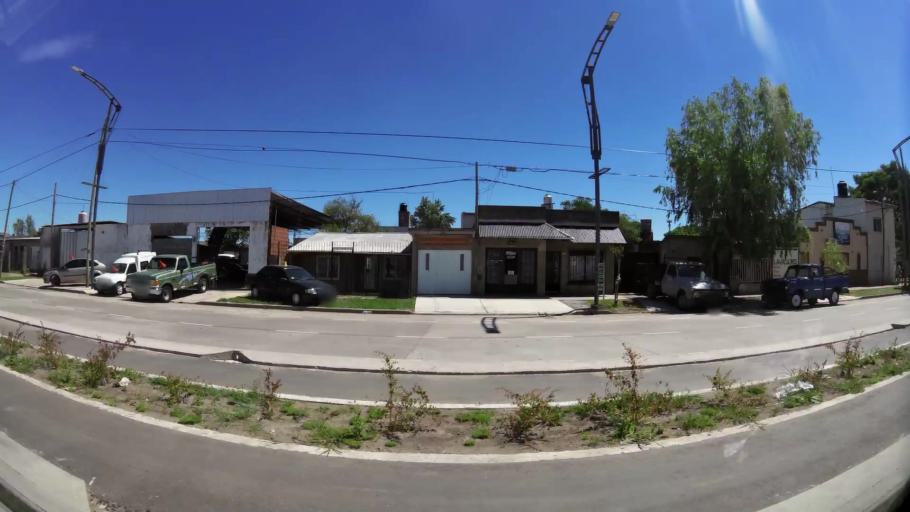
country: AR
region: Santa Fe
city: Perez
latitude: -32.9596
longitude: -60.7168
